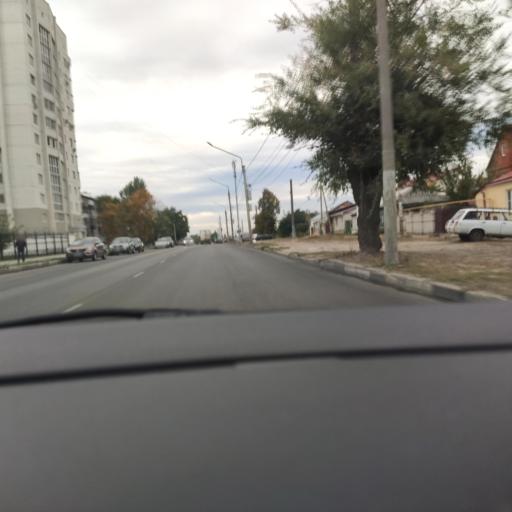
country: RU
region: Voronezj
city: Voronezh
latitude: 51.6387
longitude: 39.1746
